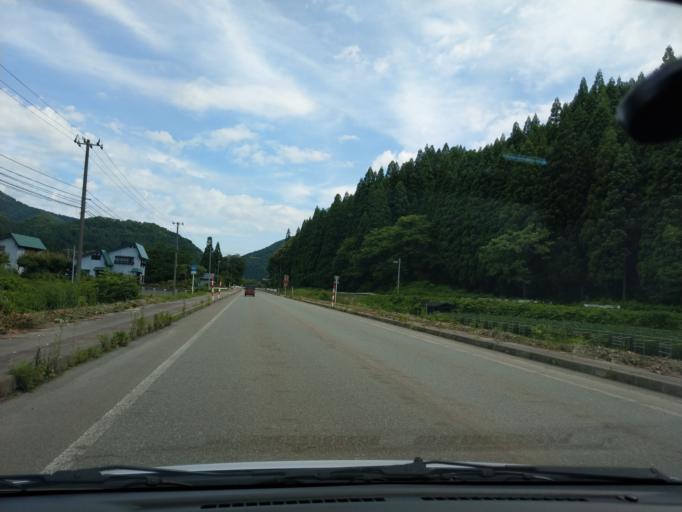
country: JP
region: Akita
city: Kakunodatemachi
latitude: 39.6865
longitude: 140.5552
